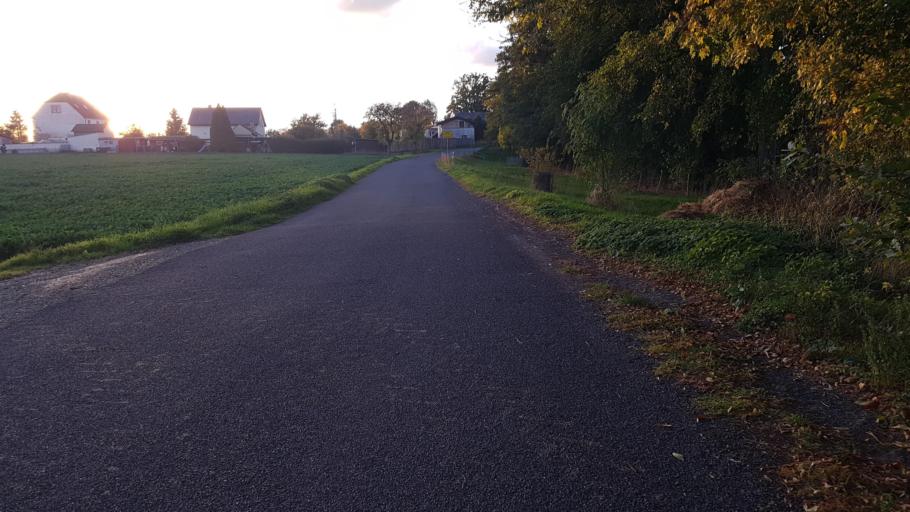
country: DE
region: Saxony
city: Priestewitz
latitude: 51.2322
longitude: 13.5388
